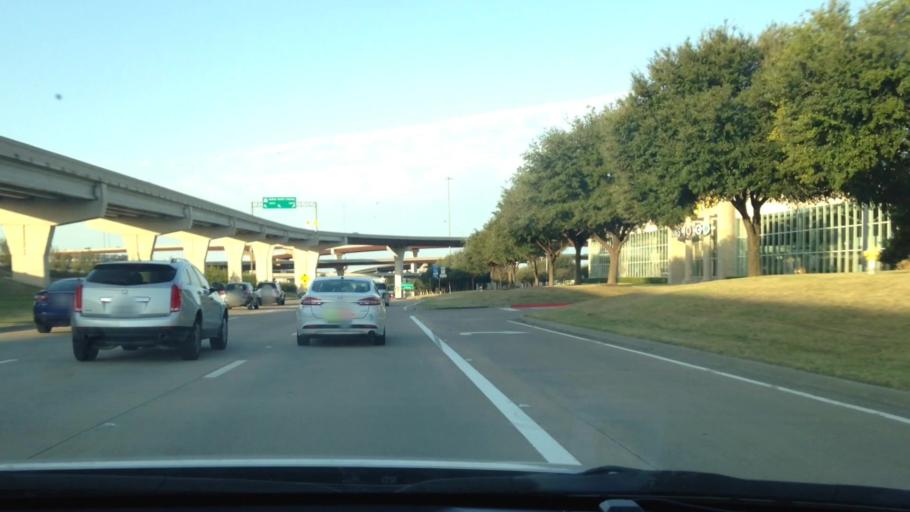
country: US
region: Texas
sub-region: Collin County
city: Frisco
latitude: 33.0935
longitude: -96.8175
